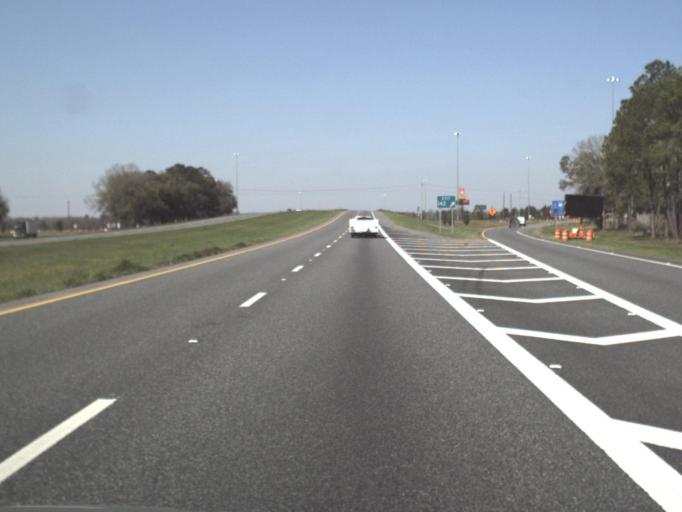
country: US
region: Florida
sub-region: Jackson County
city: Marianna
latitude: 30.7205
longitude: -85.1808
